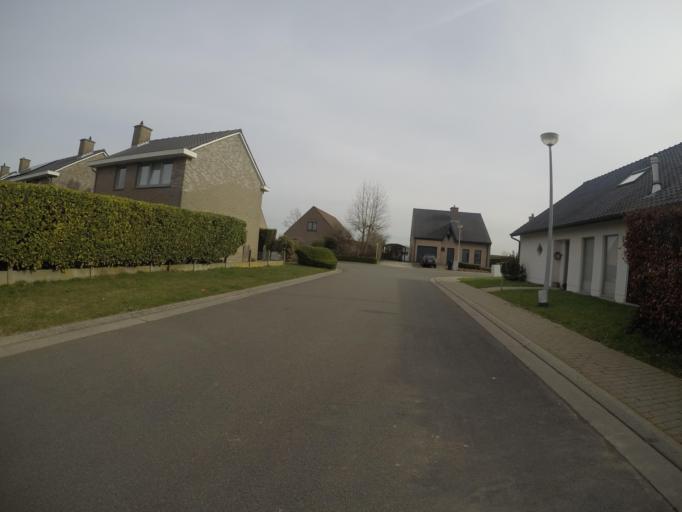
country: BE
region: Flanders
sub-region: Provincie Oost-Vlaanderen
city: Sint-Maria-Lierde
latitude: 50.8043
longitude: 3.8277
